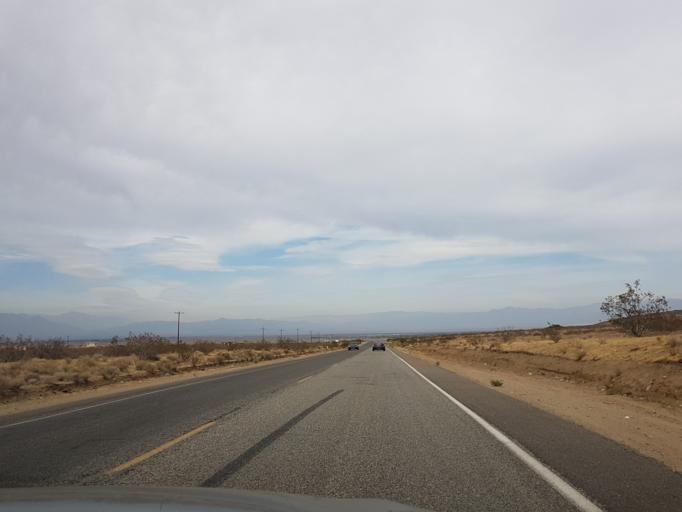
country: US
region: California
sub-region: Kern County
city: Ridgecrest
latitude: 35.5632
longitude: -117.7139
